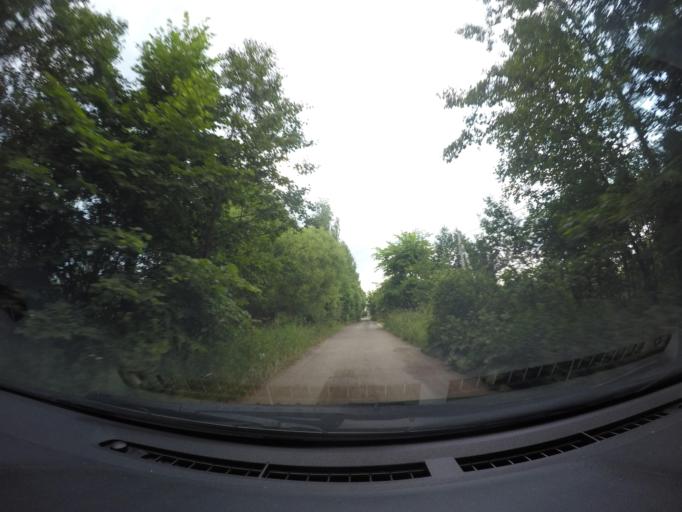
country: RU
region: Moskovskaya
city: Krasnyy Tkach
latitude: 55.4194
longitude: 39.2350
